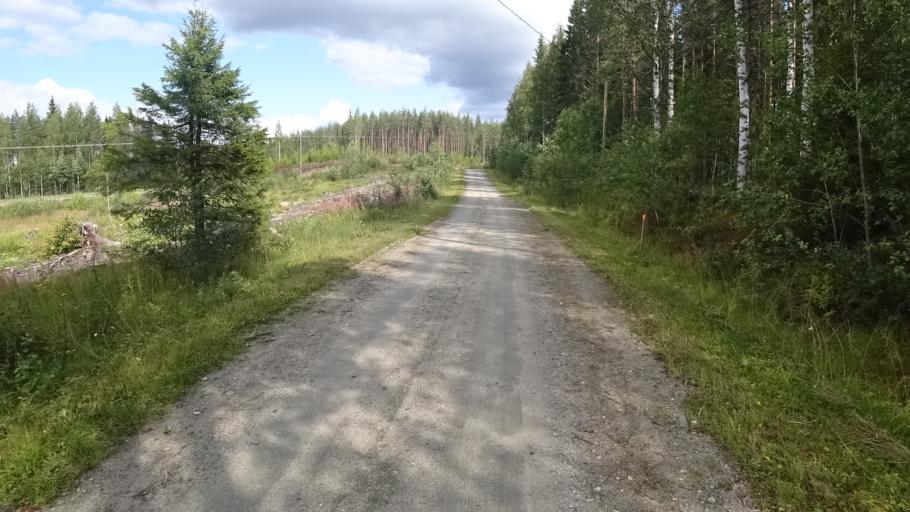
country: FI
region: North Karelia
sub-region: Joensuu
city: Ilomantsi
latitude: 62.6239
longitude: 31.2507
